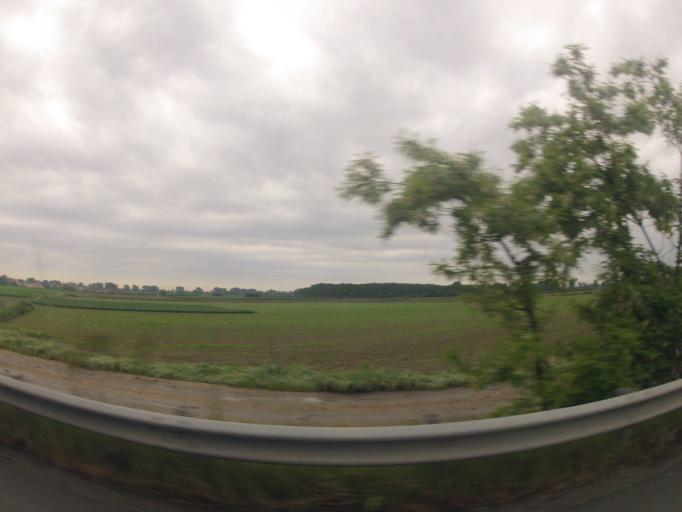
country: IT
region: Piedmont
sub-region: Provincia di Torino
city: La Loggia
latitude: 44.9565
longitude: 7.6808
